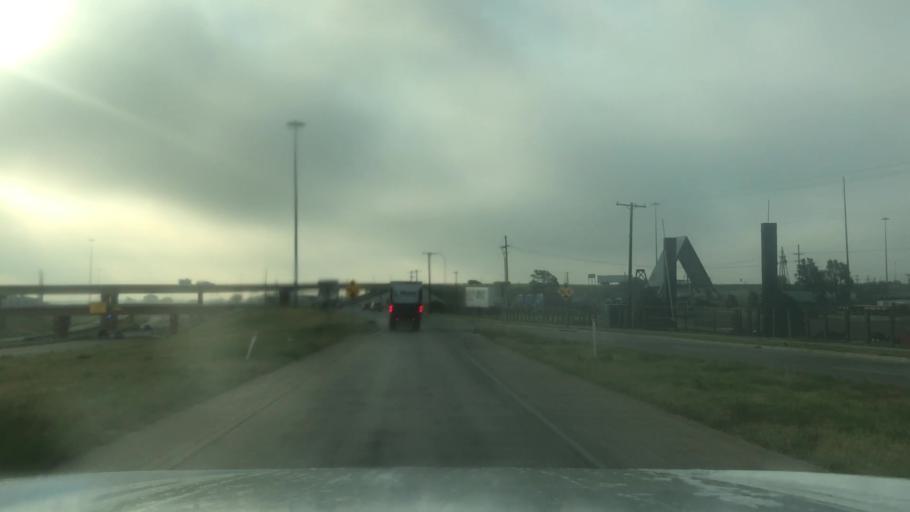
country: US
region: Texas
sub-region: Lubbock County
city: Lubbock
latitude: 33.5916
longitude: -101.8425
